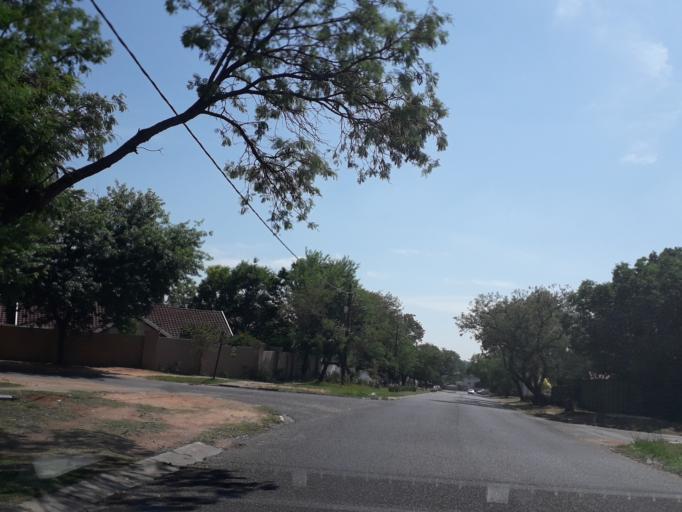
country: ZA
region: Gauteng
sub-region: City of Johannesburg Metropolitan Municipality
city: Johannesburg
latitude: -26.1071
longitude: 28.0116
